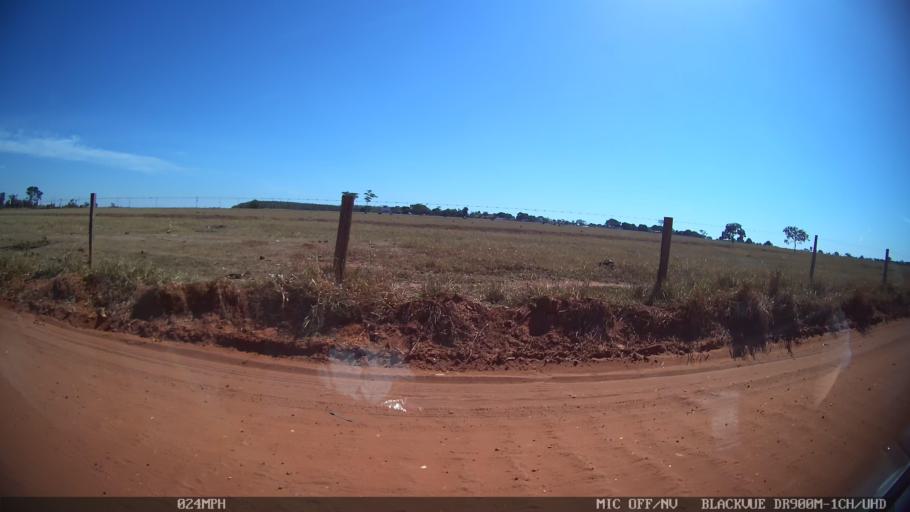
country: BR
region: Sao Paulo
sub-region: Sao Jose Do Rio Preto
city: Sao Jose do Rio Preto
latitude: -20.7433
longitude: -49.4313
